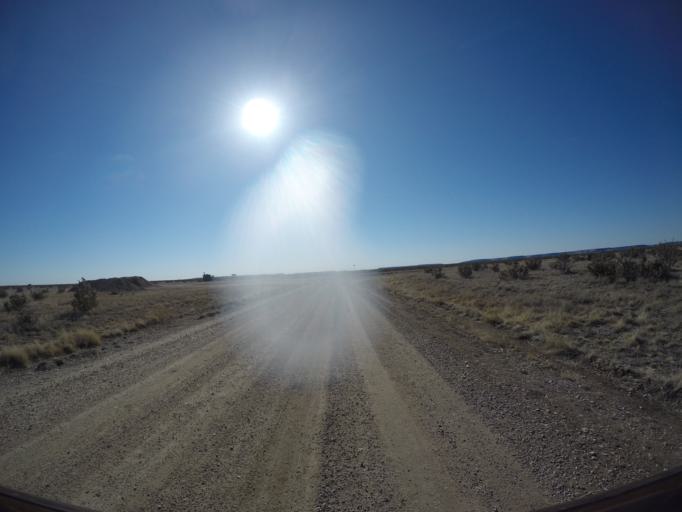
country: US
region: Colorado
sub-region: Otero County
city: La Junta
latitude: 37.6597
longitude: -103.6203
